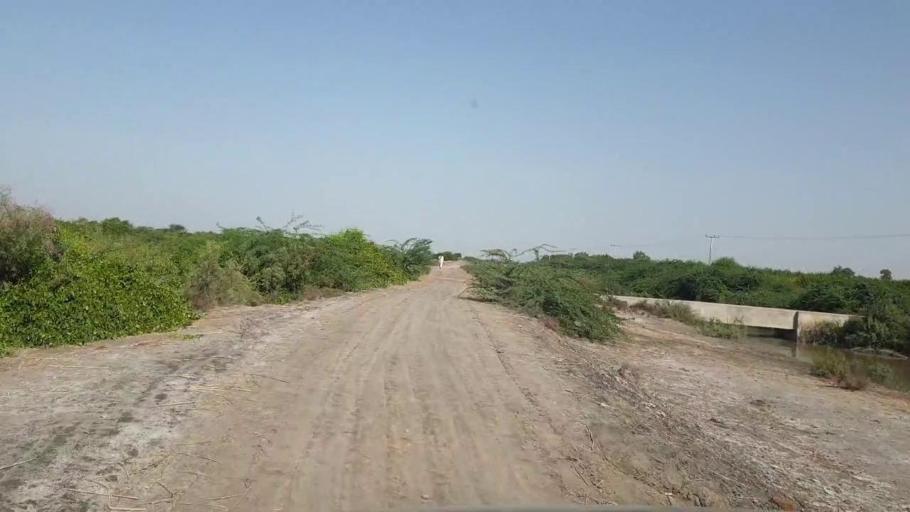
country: PK
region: Sindh
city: Tando Bago
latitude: 24.6975
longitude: 69.0703
